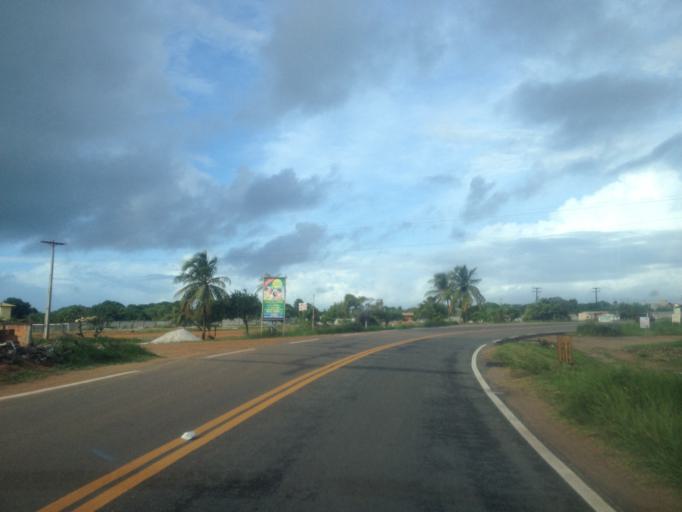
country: BR
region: Bahia
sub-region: Mata De Sao Joao
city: Mata de Sao Joao
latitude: -12.3775
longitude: -37.8866
